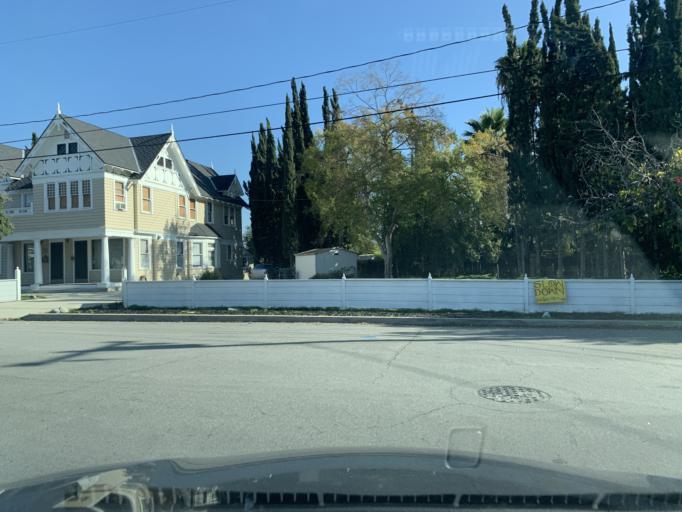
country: US
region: California
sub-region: Los Angeles County
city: Covina
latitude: 34.0838
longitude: -117.8803
